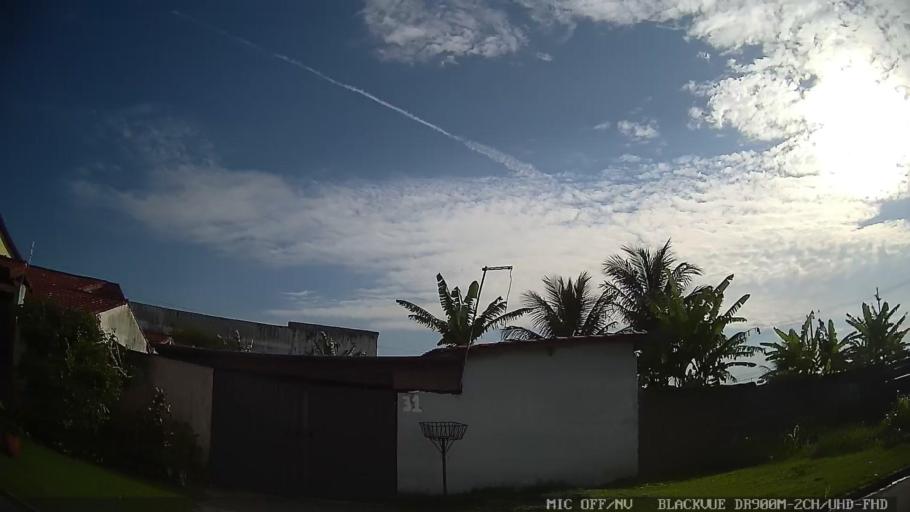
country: BR
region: Sao Paulo
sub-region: Caraguatatuba
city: Caraguatatuba
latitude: -23.6590
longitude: -45.4302
